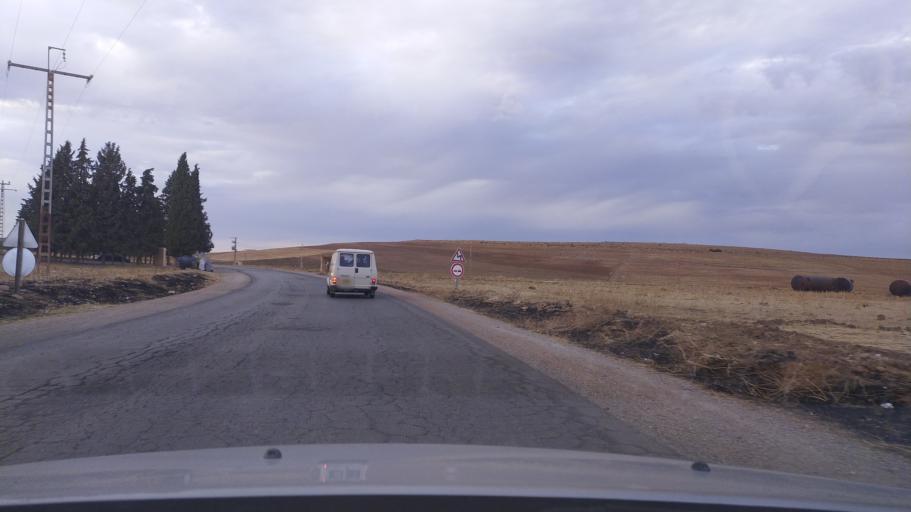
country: DZ
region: Tiaret
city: Frenda
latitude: 35.0259
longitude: 1.0988
